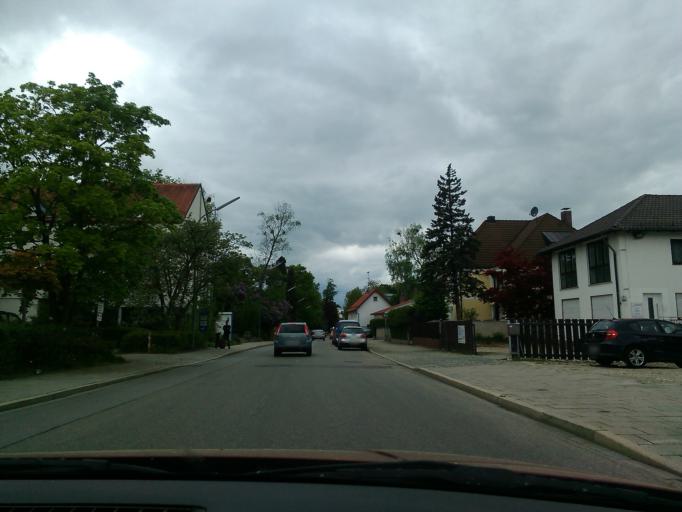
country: DE
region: Bavaria
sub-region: Upper Bavaria
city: Planegg
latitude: 48.1022
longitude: 11.4261
